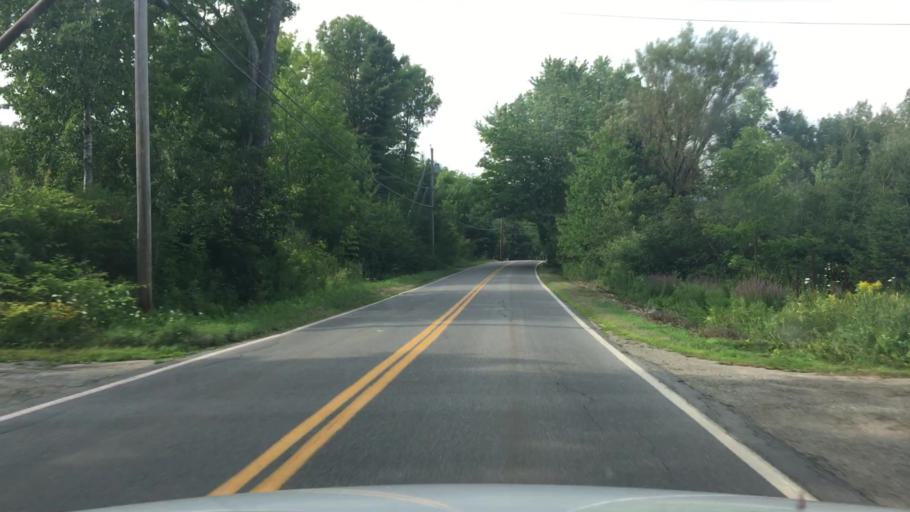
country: US
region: Maine
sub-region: Lincoln County
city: Waldoboro
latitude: 44.1493
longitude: -69.3742
